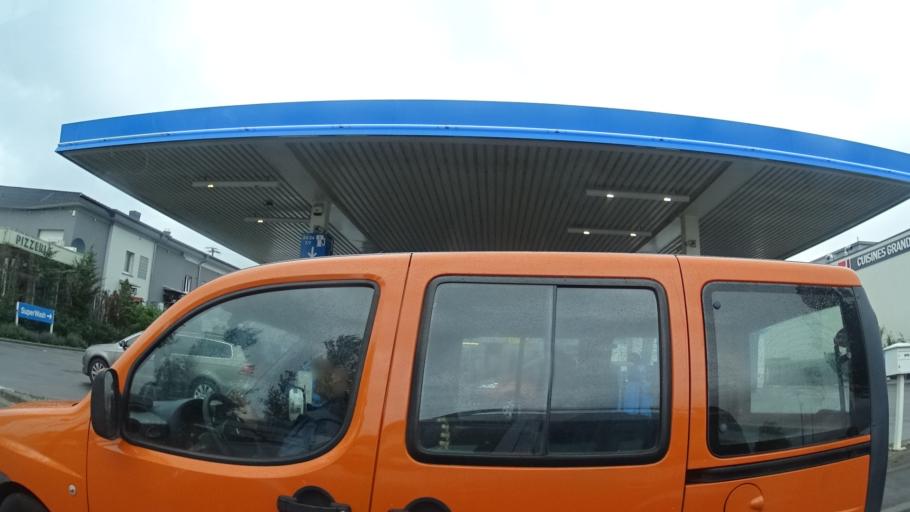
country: LU
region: Luxembourg
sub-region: Canton d'Esch-sur-Alzette
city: Schifflange
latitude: 49.5227
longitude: 6.0083
